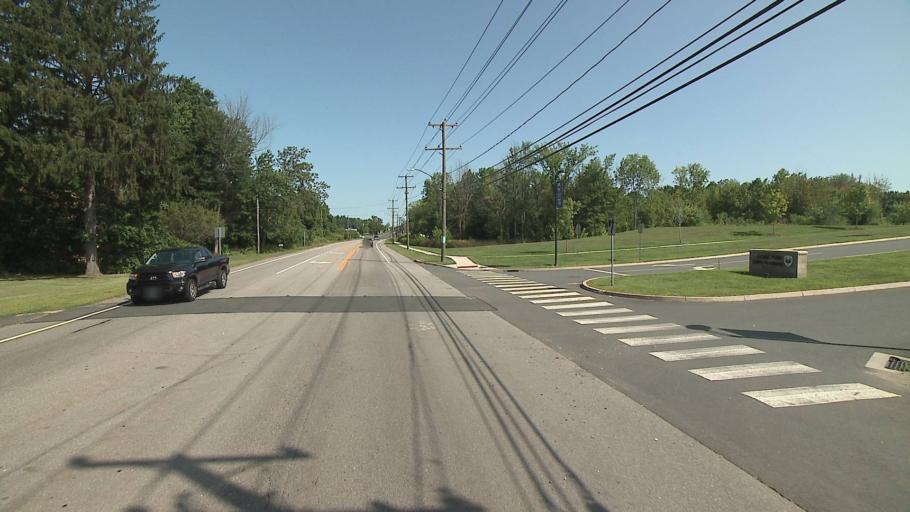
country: US
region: Connecticut
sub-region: Hartford County
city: Enfield
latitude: 41.9482
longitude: -72.6021
